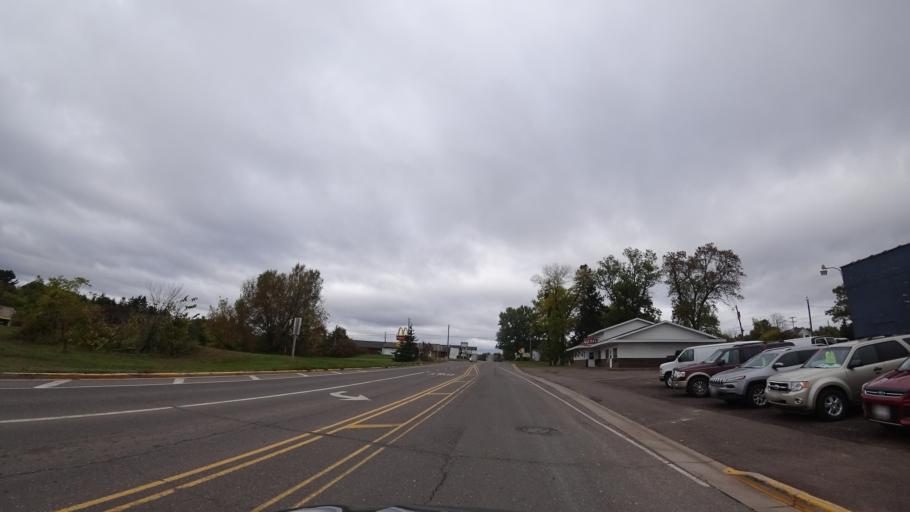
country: US
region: Wisconsin
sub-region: Rusk County
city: Ladysmith
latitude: 45.4651
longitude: -91.1110
